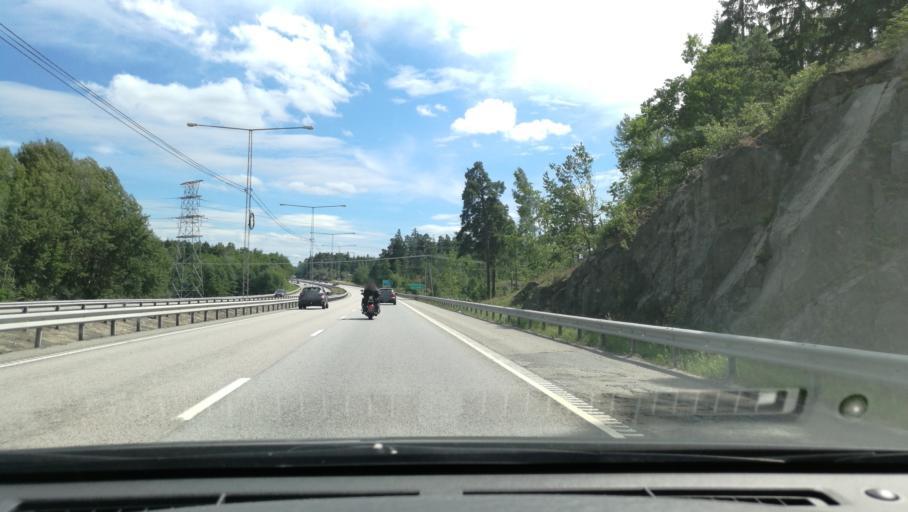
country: SE
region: Stockholm
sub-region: Jarfalla Kommun
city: Jakobsberg
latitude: 59.4591
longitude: 17.8267
